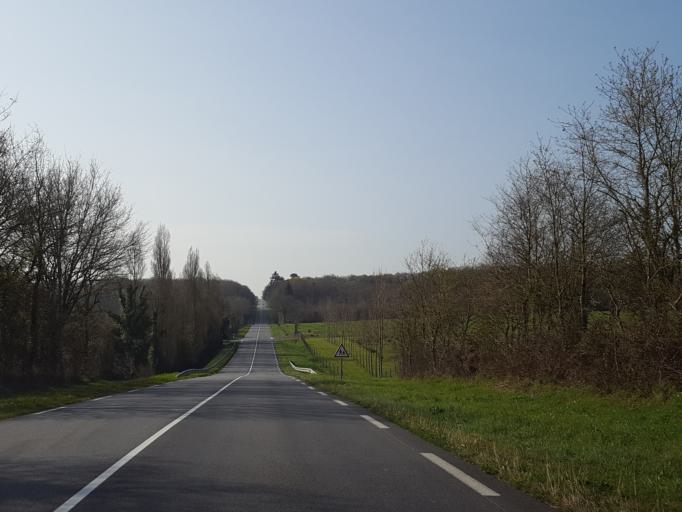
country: FR
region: Pays de la Loire
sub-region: Departement de la Vendee
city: Rocheserviere
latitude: 46.9074
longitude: -1.5035
